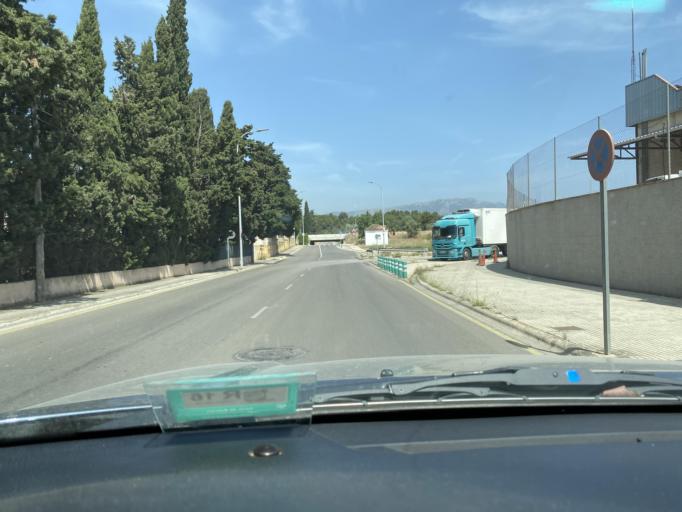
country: ES
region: Balearic Islands
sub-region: Illes Balears
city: Marratxi
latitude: 39.6216
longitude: 2.7124
